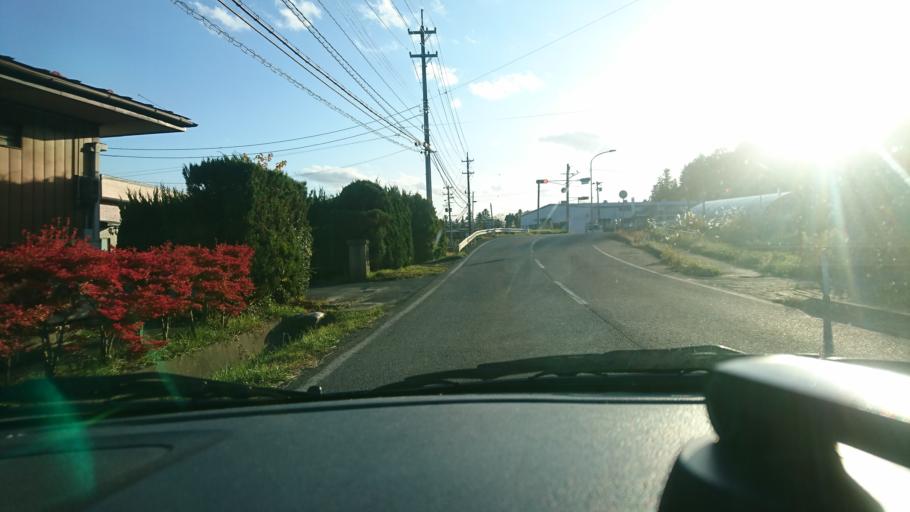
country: JP
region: Iwate
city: Ichinoseki
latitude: 38.8512
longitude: 141.1803
